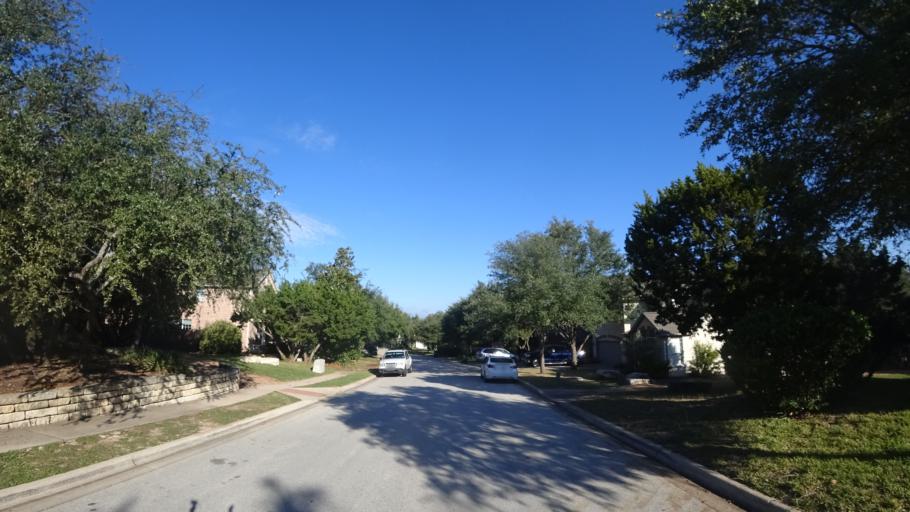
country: US
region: Texas
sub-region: Travis County
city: Hudson Bend
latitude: 30.3707
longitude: -97.8983
